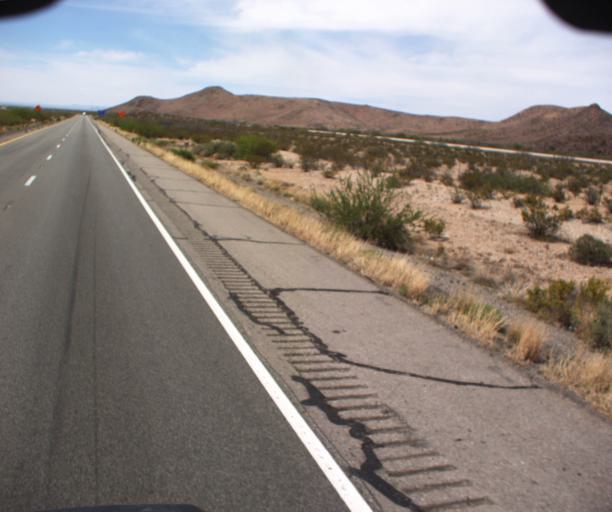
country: US
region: New Mexico
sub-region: Hidalgo County
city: Lordsburg
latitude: 32.2346
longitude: -109.0725
